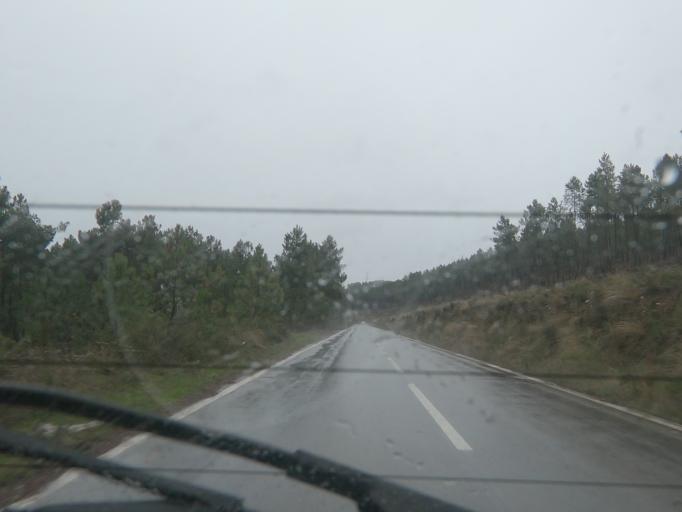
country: PT
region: Vila Real
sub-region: Sabrosa
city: Vilela
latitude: 41.2129
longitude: -7.6763
